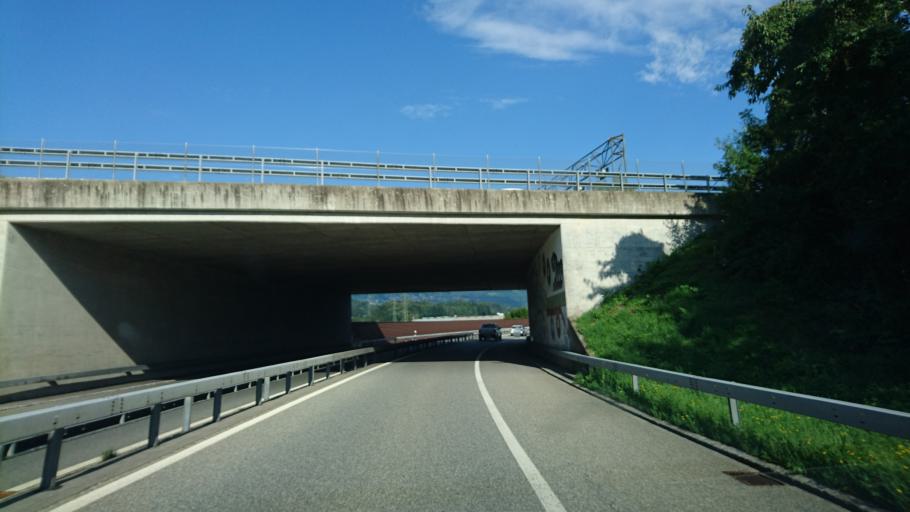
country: CH
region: Saint Gallen
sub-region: Wahlkreis See-Gaster
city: Schmerikon
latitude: 47.2280
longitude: 8.9619
